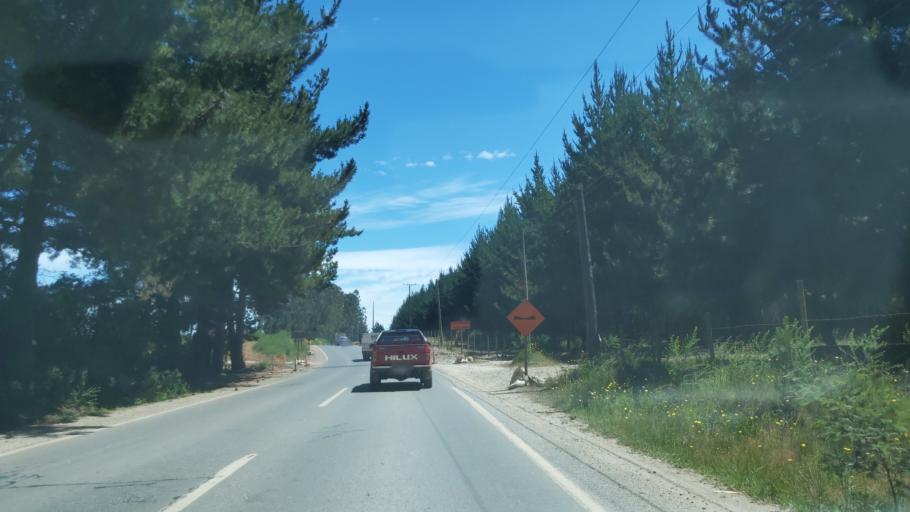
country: CL
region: Maule
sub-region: Provincia de Talca
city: Constitucion
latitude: -35.3943
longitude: -72.4284
